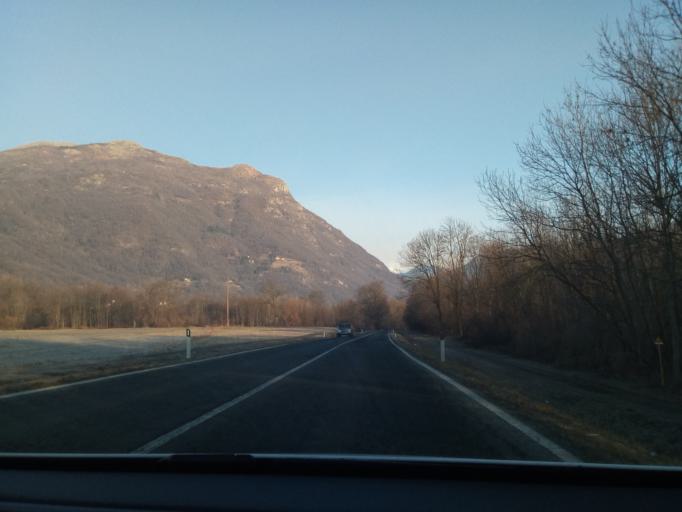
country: IT
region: Piedmont
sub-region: Provincia di Torino
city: Lessolo
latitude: 45.4862
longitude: 7.8289
